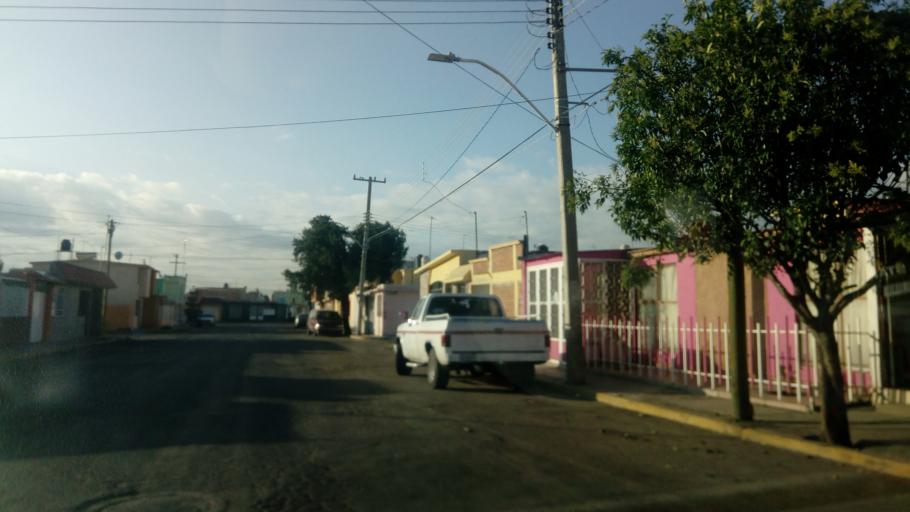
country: MX
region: Durango
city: Victoria de Durango
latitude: 24.0479
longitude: -104.6191
